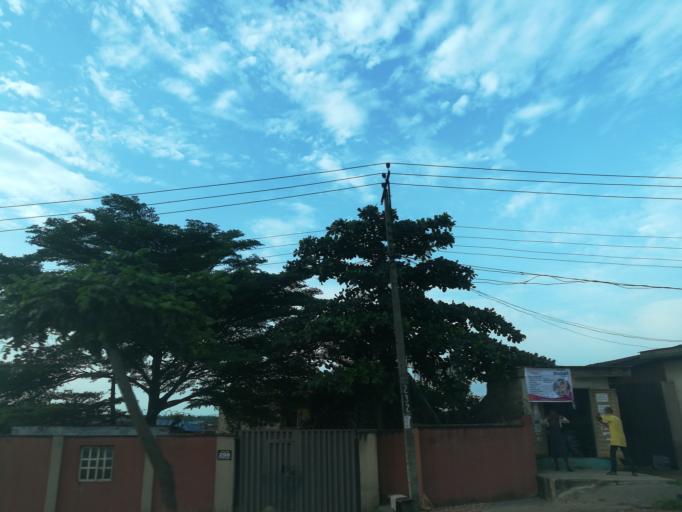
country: NG
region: Lagos
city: Ebute Ikorodu
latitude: 6.6197
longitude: 3.4741
